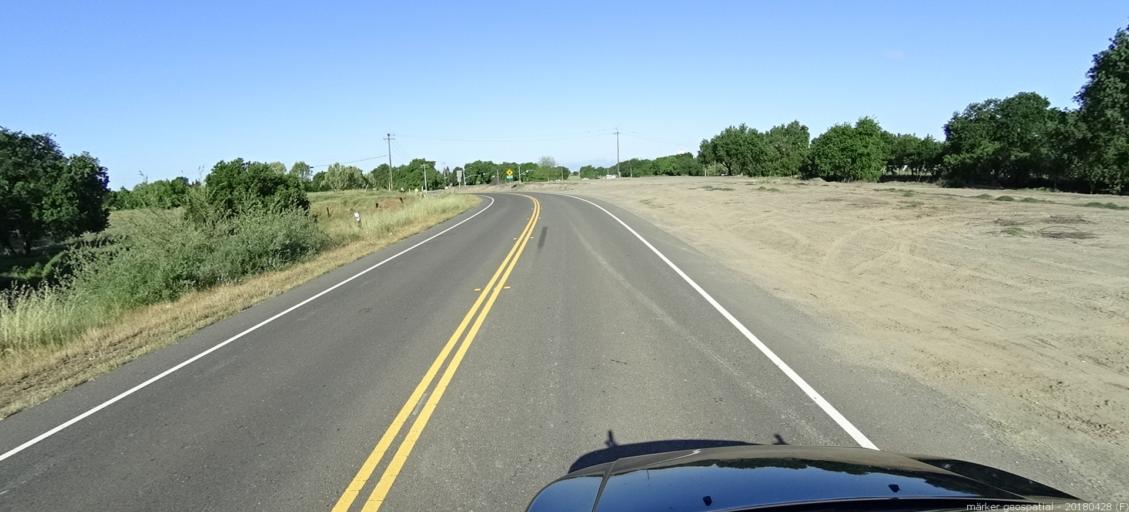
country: US
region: California
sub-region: Yolo County
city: West Sacramento
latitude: 38.5600
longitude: -121.5260
